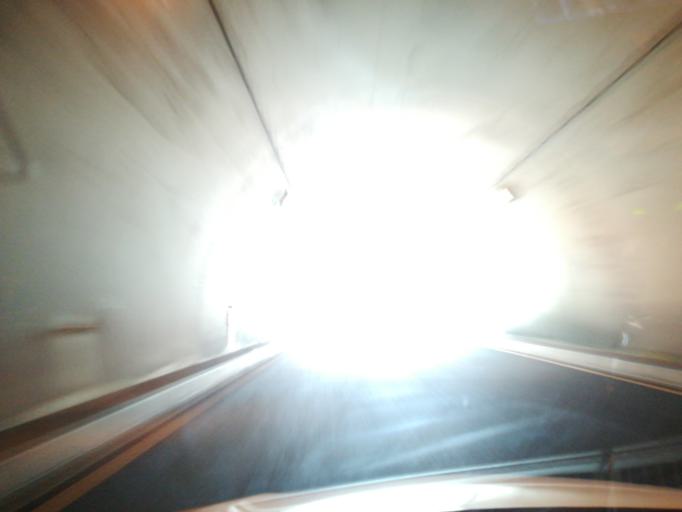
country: JP
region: Kochi
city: Kochi-shi
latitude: 33.7757
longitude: 133.6607
